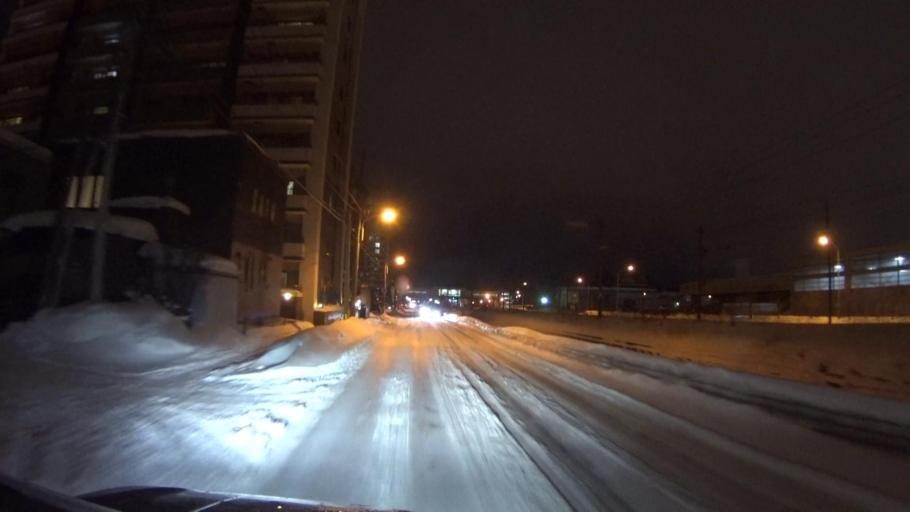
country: JP
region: Hokkaido
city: Sapporo
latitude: 43.0978
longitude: 141.2802
